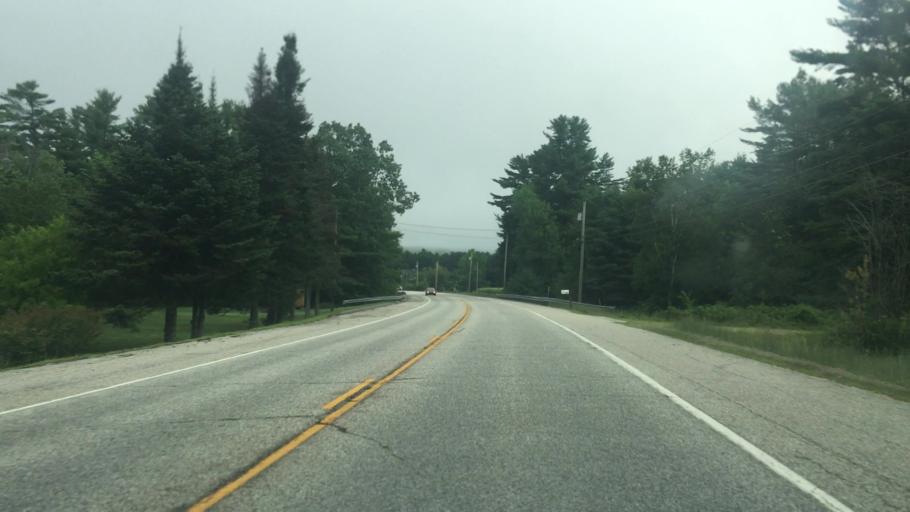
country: US
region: Maine
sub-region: Oxford County
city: Paris
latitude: 44.2747
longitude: -70.5141
